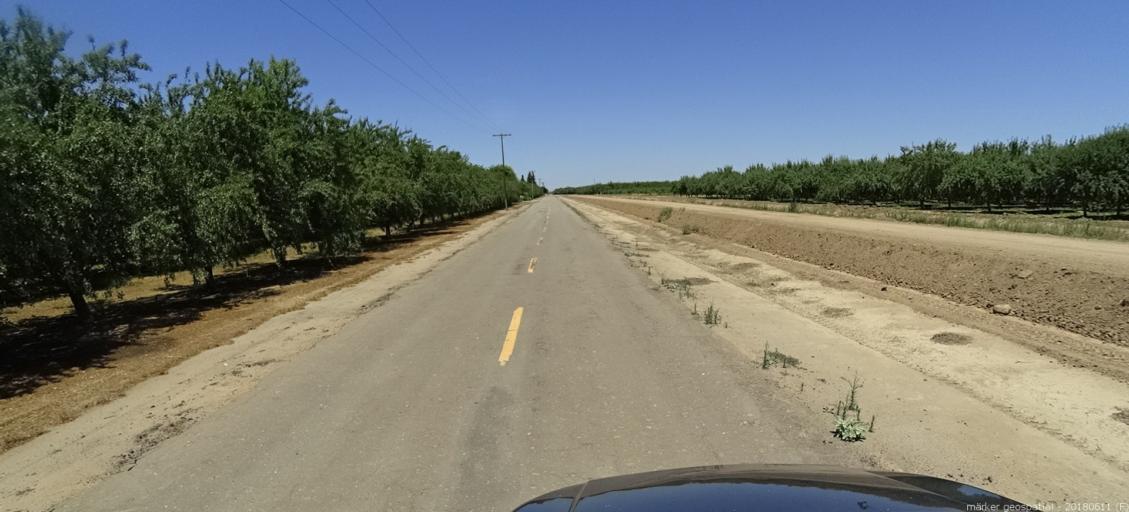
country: US
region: California
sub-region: Madera County
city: Fairmead
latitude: 37.0353
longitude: -120.1932
